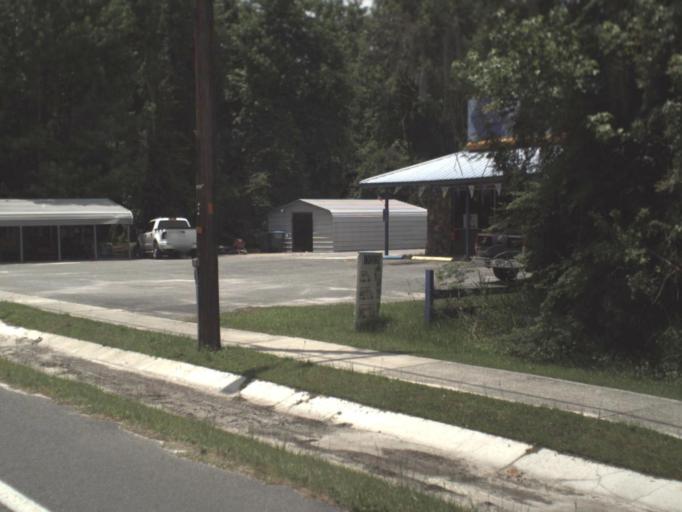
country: US
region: Florida
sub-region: Suwannee County
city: Wellborn
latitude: 30.3299
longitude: -82.7495
